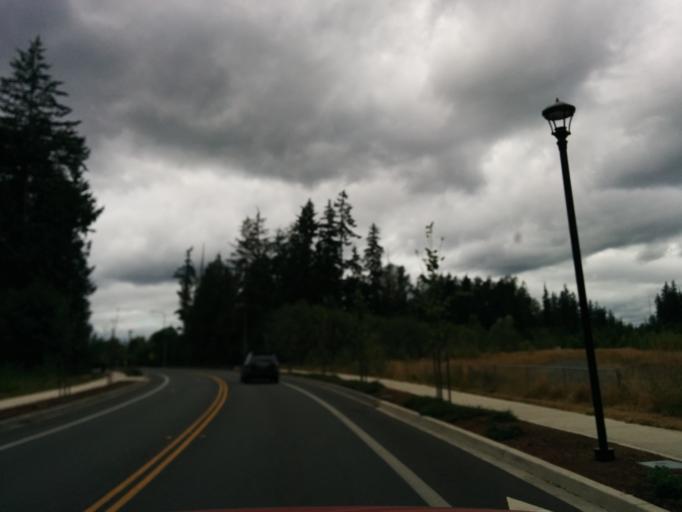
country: US
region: Washington
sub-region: King County
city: Union Hill-Novelty Hill
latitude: 47.6853
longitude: -122.0306
